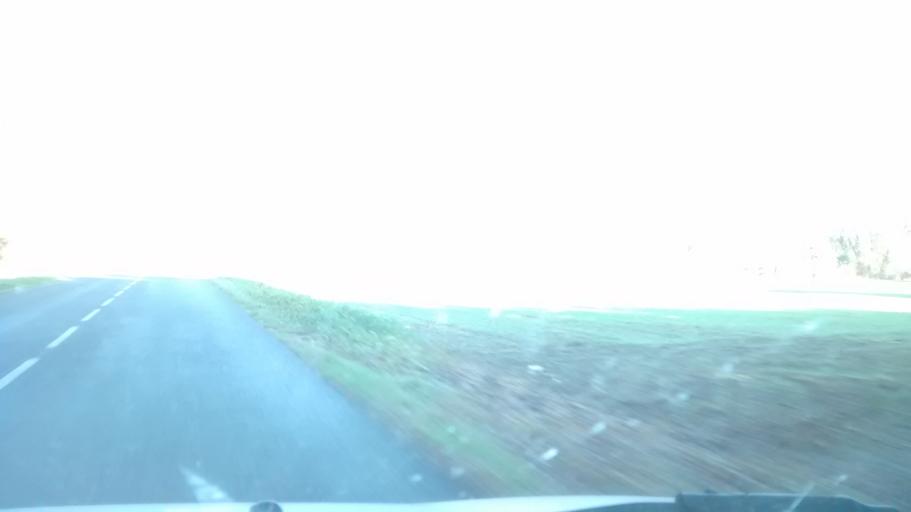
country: FR
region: Centre
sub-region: Departement d'Indre-et-Loire
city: Reugny
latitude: 47.4733
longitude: 0.8807
